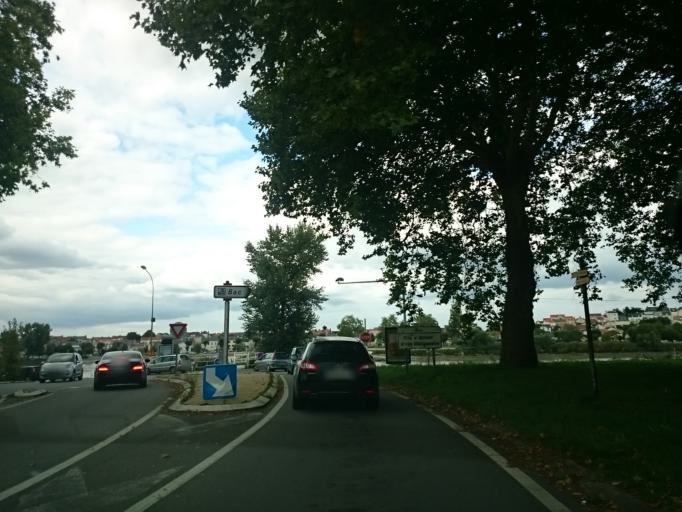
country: FR
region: Pays de la Loire
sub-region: Departement de la Loire-Atlantique
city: Indre
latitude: 47.1949
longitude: -1.6754
